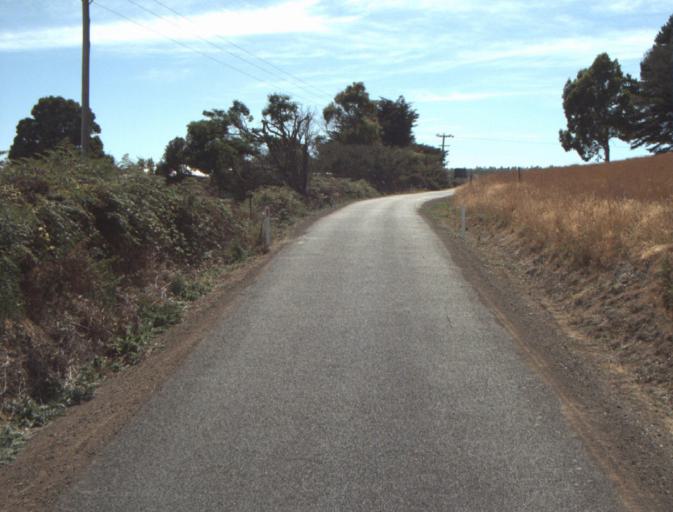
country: AU
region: Tasmania
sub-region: Launceston
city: Mayfield
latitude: -41.2311
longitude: 147.2441
